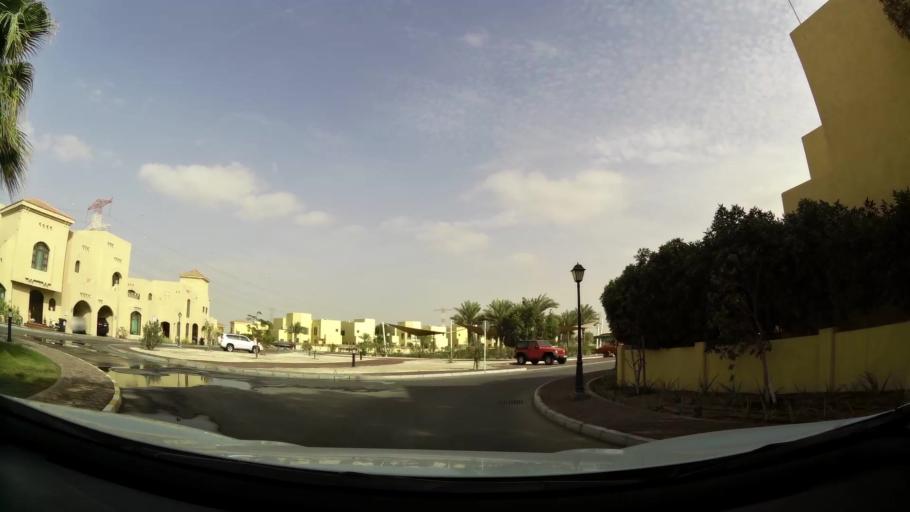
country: AE
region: Abu Dhabi
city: Abu Dhabi
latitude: 24.4028
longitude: 54.5314
